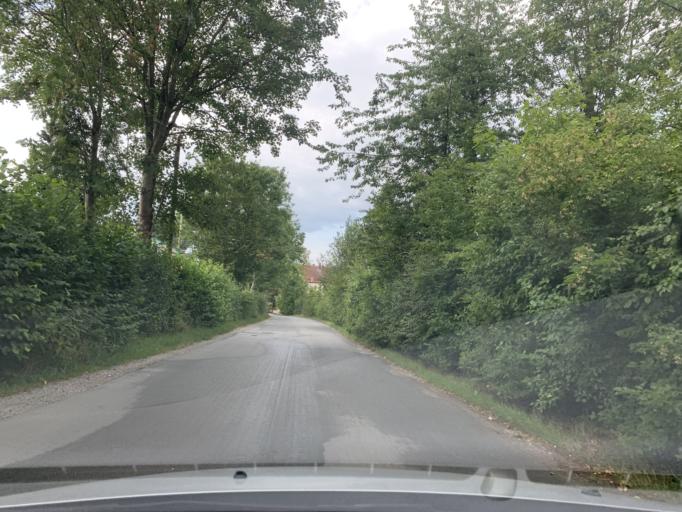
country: DE
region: Bavaria
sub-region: Upper Bavaria
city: Muehldorf
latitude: 48.2493
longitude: 12.5491
